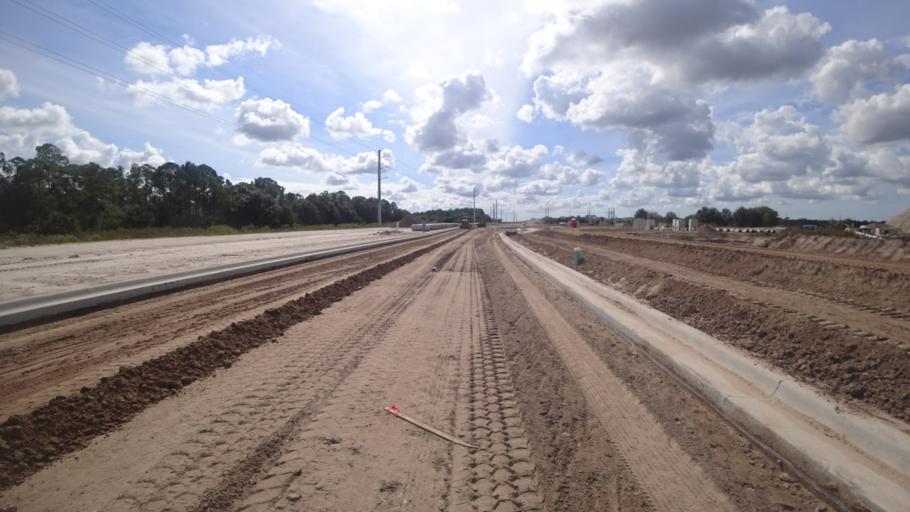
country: US
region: Florida
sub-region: Sarasota County
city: The Meadows
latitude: 27.4223
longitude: -82.3523
